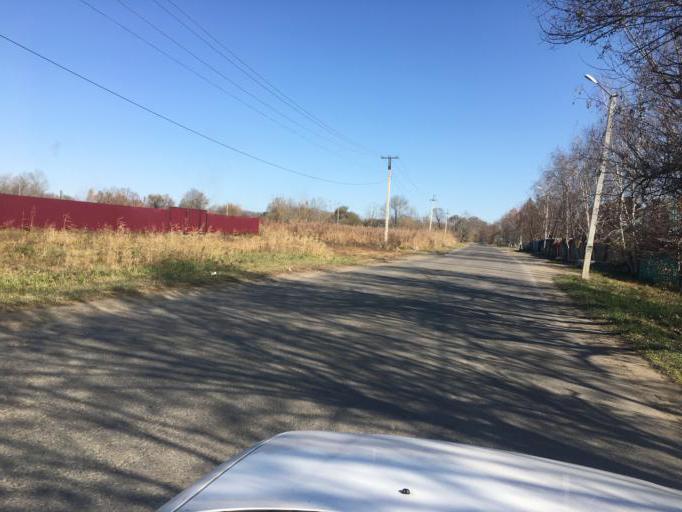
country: RU
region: Primorskiy
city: Dal'nerechensk
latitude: 45.9327
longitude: 133.7496
